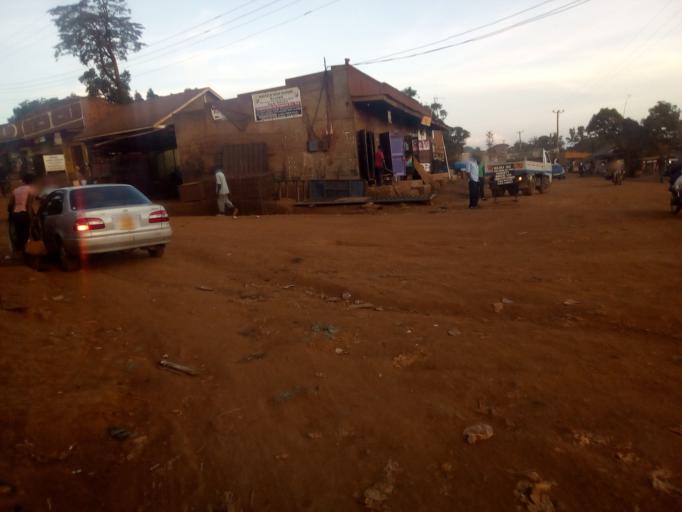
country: UG
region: Central Region
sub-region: Wakiso District
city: Kajansi
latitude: 0.2364
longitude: 32.5760
